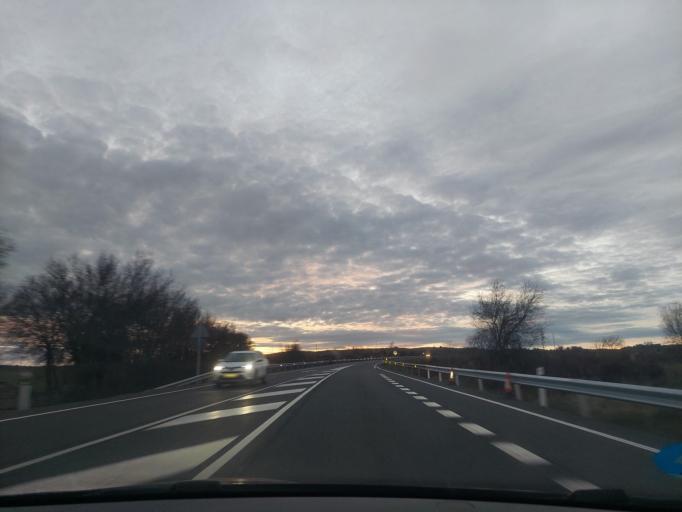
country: ES
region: Castille and Leon
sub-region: Provincia de Segovia
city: Santo Domingo de Piron
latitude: 41.0091
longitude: -3.9863
